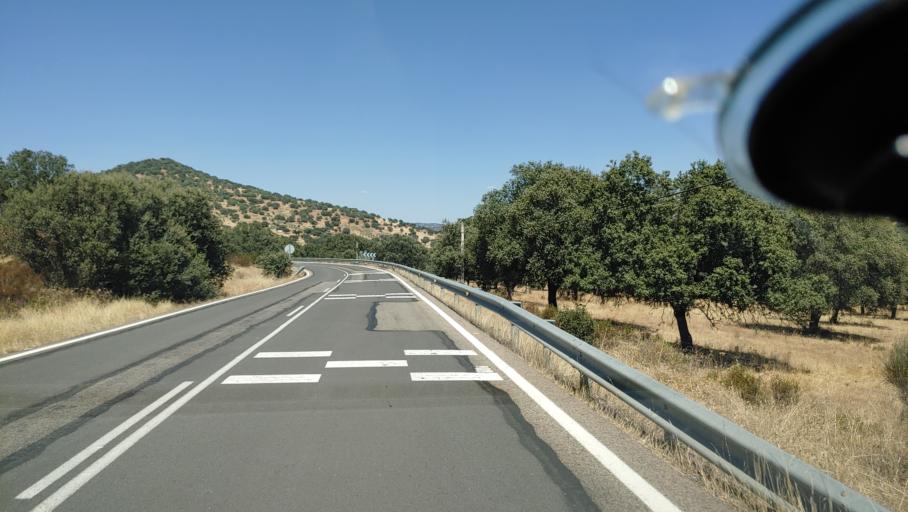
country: ES
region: Castille-La Mancha
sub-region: Provincia de Ciudad Real
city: Alamillo
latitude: 38.7517
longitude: -4.6999
